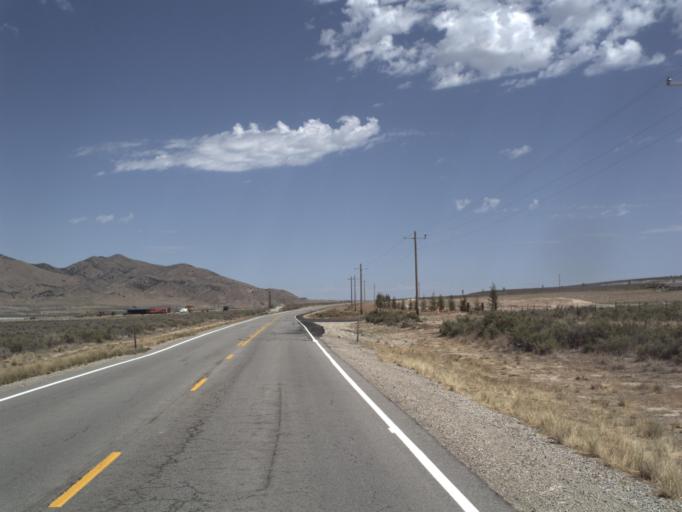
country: US
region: Utah
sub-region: Tooele County
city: Tooele
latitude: 40.3997
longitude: -112.3860
